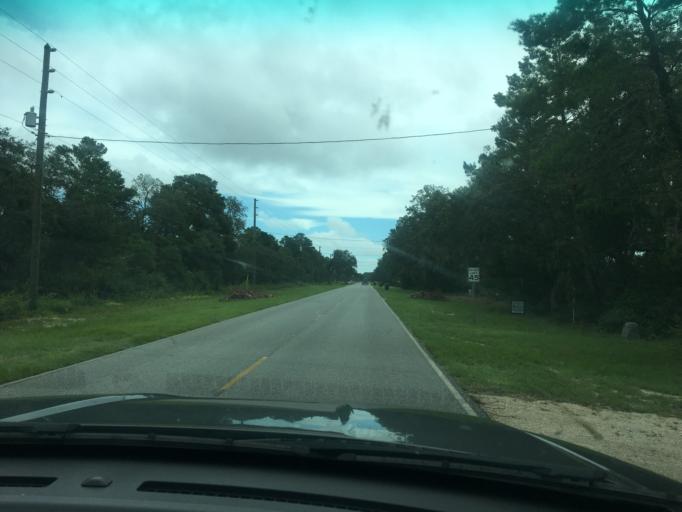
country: US
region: Florida
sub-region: Wakulla County
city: Crawfordville
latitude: 29.9088
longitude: -84.3598
